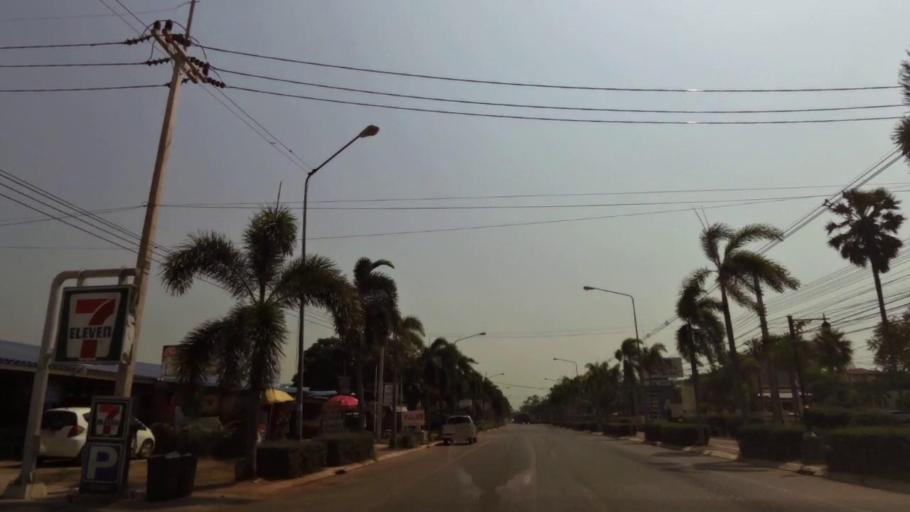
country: TH
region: Chanthaburi
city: Tha Mai
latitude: 12.5534
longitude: 101.9219
